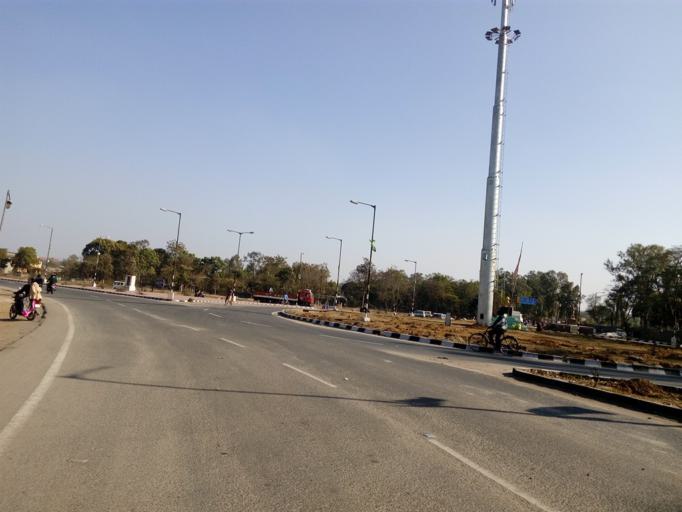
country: IN
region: Jharkhand
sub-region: Ranchi
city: Ranchi
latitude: 23.3550
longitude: 85.3641
